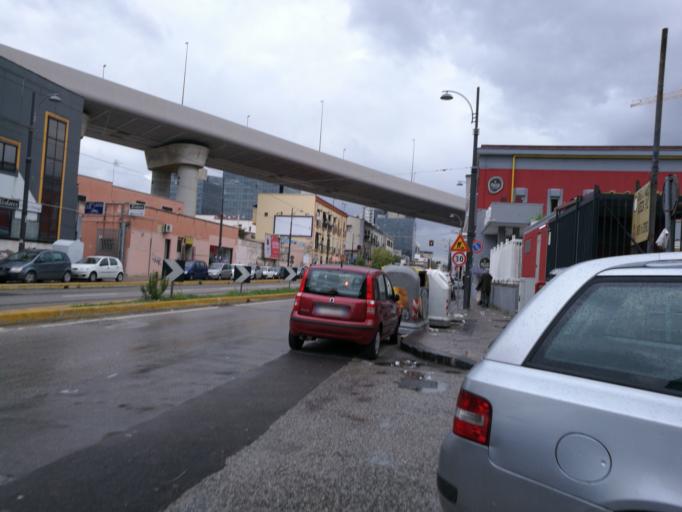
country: IT
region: Campania
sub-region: Provincia di Napoli
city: Casavatore
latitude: 40.8628
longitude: 14.2831
